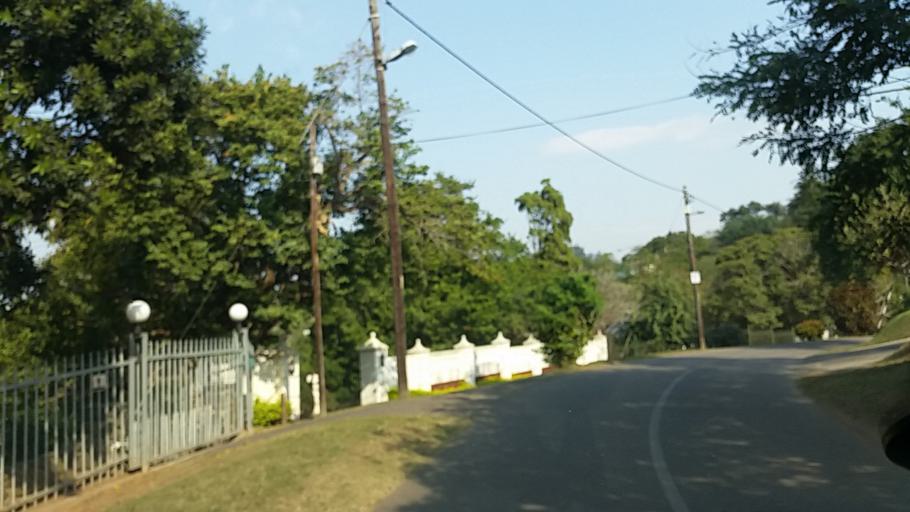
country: ZA
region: KwaZulu-Natal
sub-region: eThekwini Metropolitan Municipality
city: Berea
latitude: -29.8388
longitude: 30.9474
